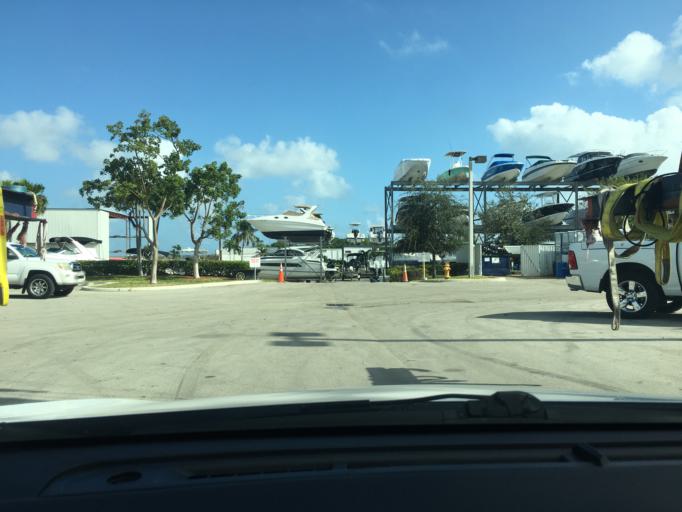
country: US
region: Florida
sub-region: Broward County
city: Dania Beach
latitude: 26.0650
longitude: -80.1676
